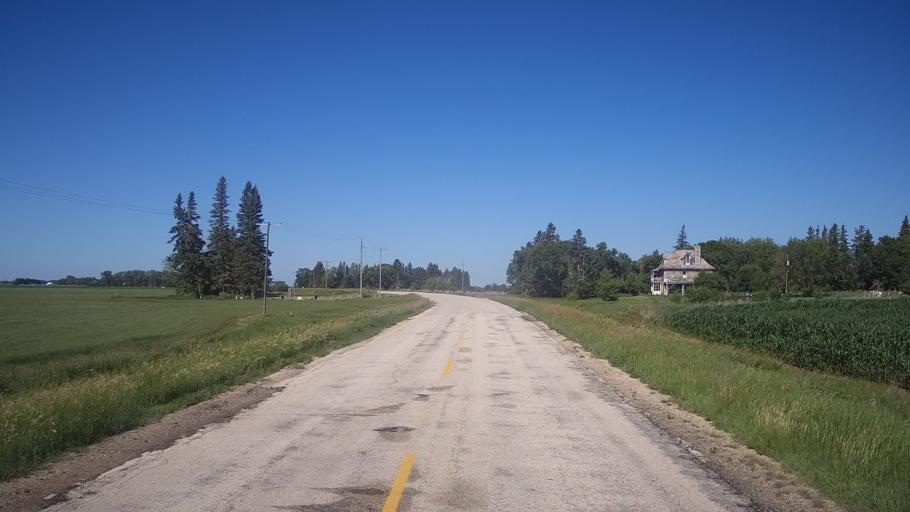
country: CA
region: Manitoba
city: Portage la Prairie
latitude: 50.0437
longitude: -98.0550
